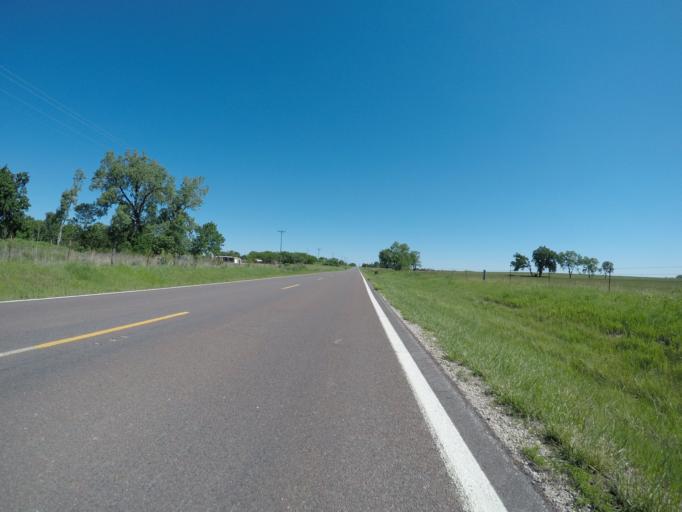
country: US
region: Kansas
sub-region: Wabaunsee County
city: Alma
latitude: 38.8470
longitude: -96.0947
